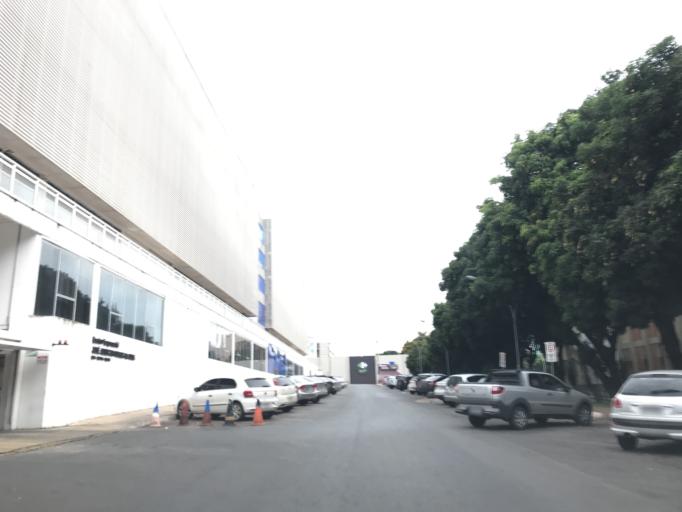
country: BR
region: Federal District
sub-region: Brasilia
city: Brasilia
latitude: -15.7523
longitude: -47.8940
